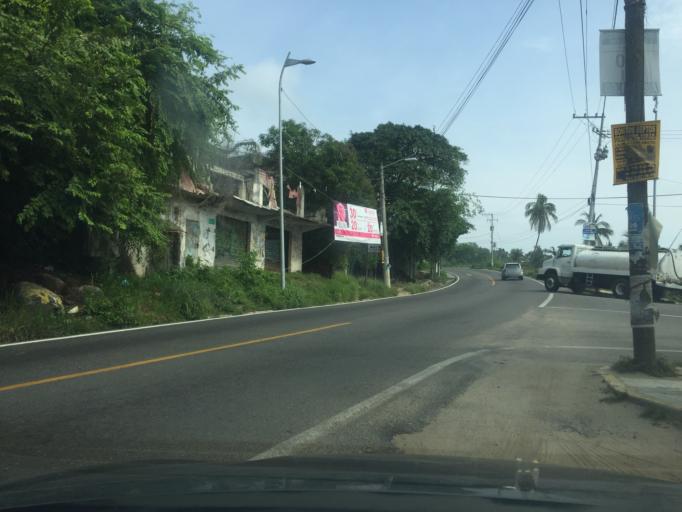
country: MX
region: Guerrero
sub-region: Coyuca de Benitez
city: Colonia Luces en el Mar
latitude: 16.8971
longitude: -99.9613
